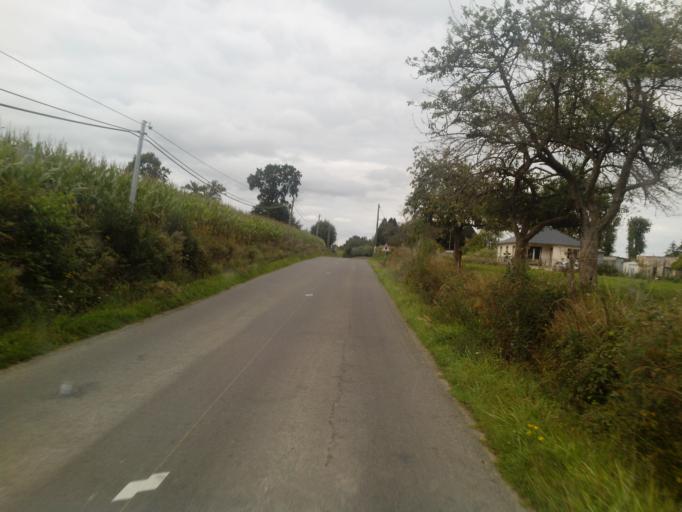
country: FR
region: Brittany
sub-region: Departement d'Ille-et-Vilaine
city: Melesse
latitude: 48.2251
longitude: -1.6894
